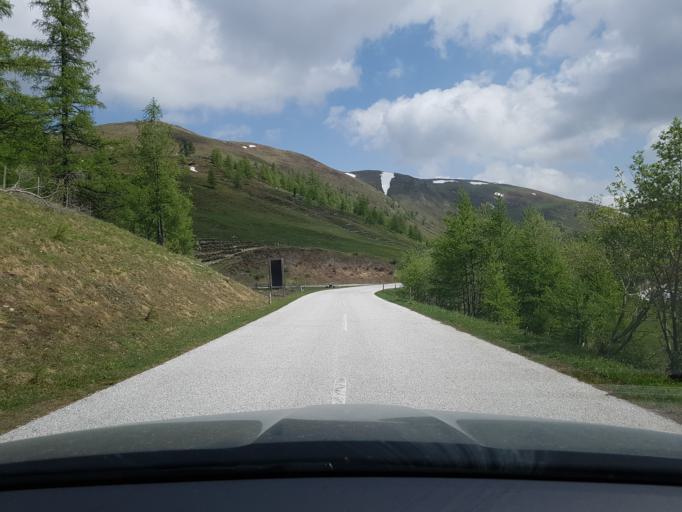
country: AT
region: Salzburg
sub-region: Politischer Bezirk Tamsweg
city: Thomatal
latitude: 46.9409
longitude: 13.7430
